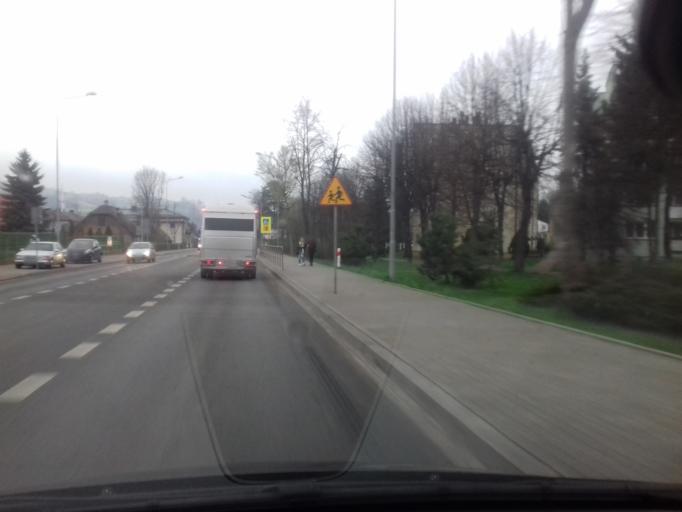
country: PL
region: Lesser Poland Voivodeship
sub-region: Powiat limanowski
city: Limanowa
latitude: 49.7200
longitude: 20.4085
